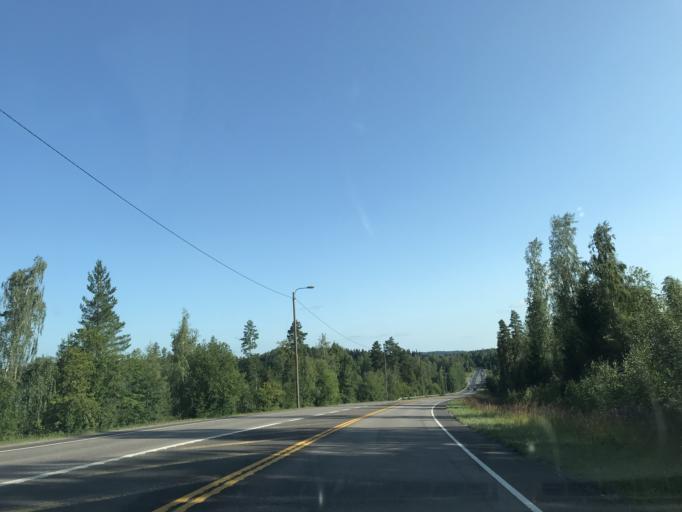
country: FI
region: Paijanne Tavastia
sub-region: Lahti
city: Lahti
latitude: 61.0464
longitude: 25.6645
